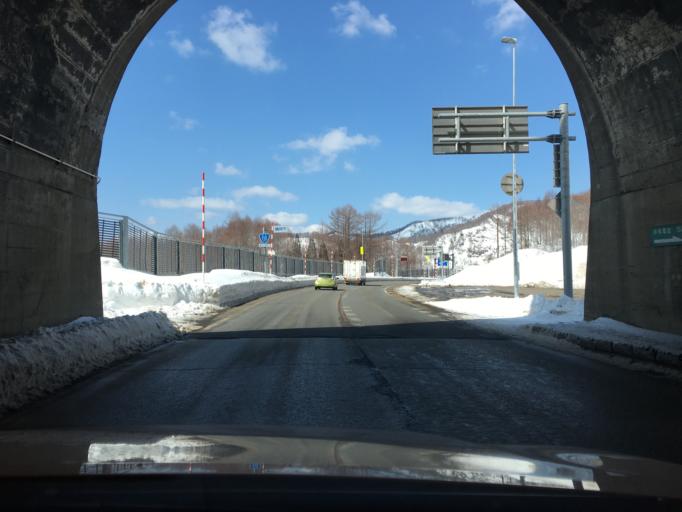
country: JP
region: Yamagata
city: Tsuruoka
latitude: 38.5027
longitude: 139.9648
